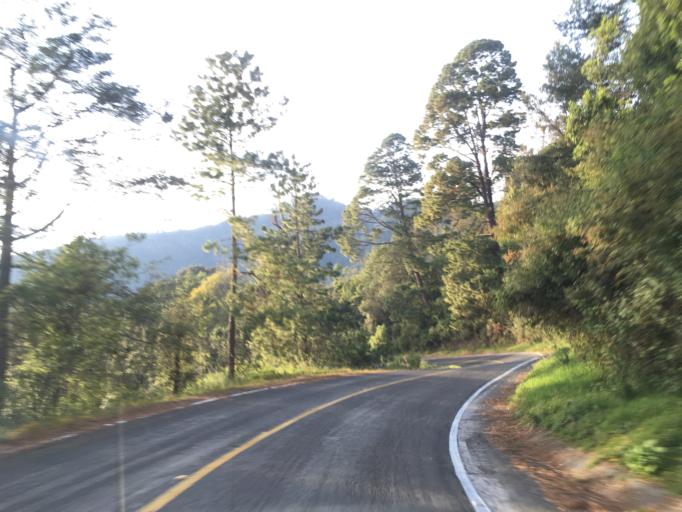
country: MX
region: Michoacan
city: Tzitzio
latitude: 19.6669
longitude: -100.9120
